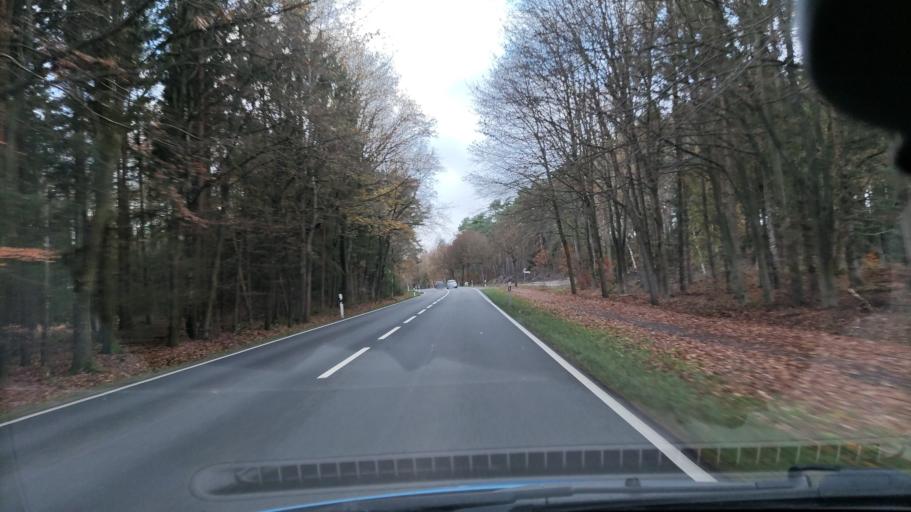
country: DE
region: Lower Saxony
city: Soltau
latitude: 53.0066
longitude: 9.8025
